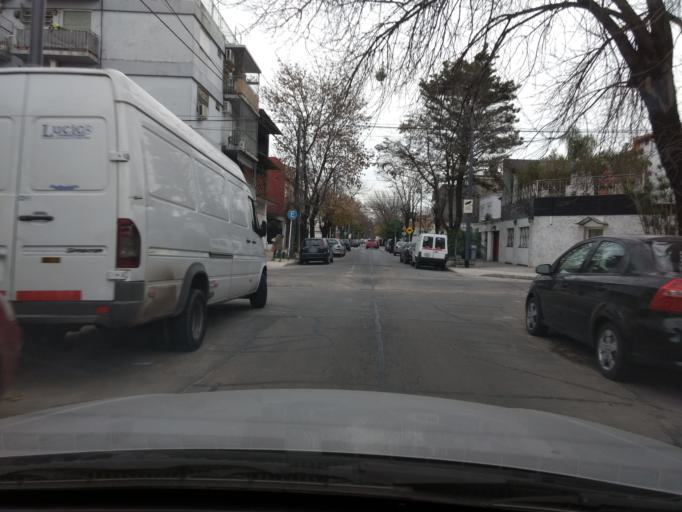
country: AR
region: Buenos Aires F.D.
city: Villa Santa Rita
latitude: -34.6240
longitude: -58.5141
